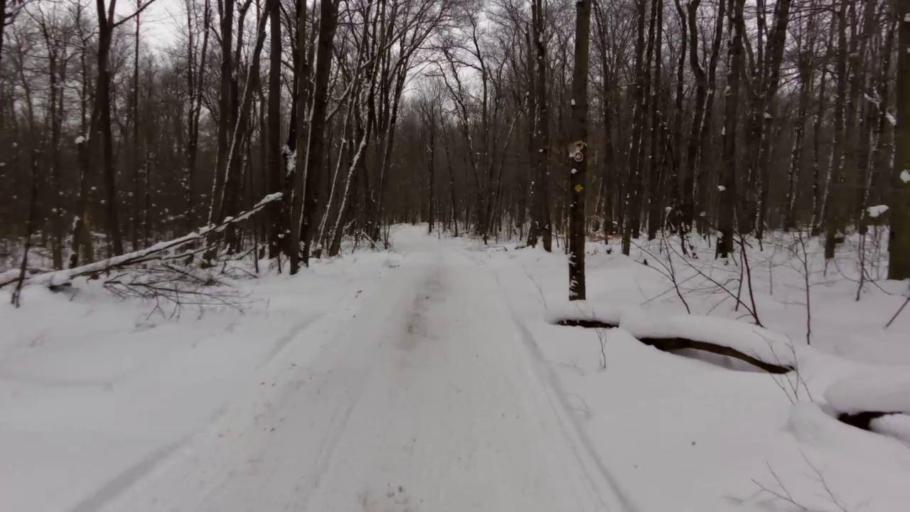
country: US
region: Pennsylvania
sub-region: McKean County
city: Bradford
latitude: 42.0074
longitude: -78.7201
